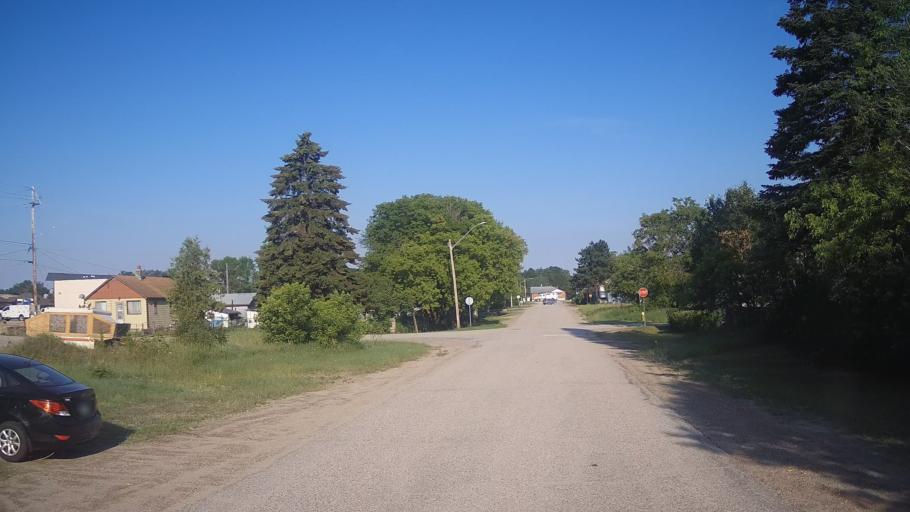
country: CA
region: Ontario
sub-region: Rainy River District
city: Atikokan
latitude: 49.4174
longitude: -91.6605
